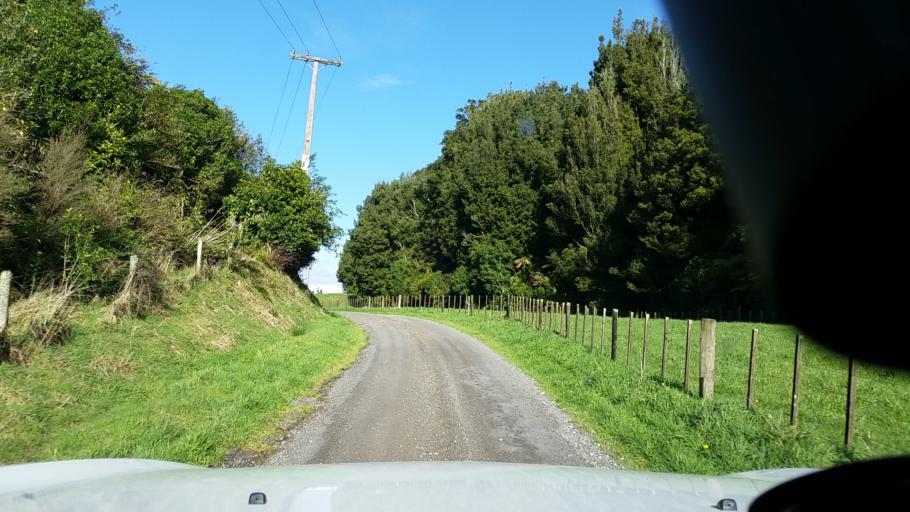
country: NZ
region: Bay of Plenty
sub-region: Rotorua District
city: Rotorua
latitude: -38.1016
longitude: 176.0679
